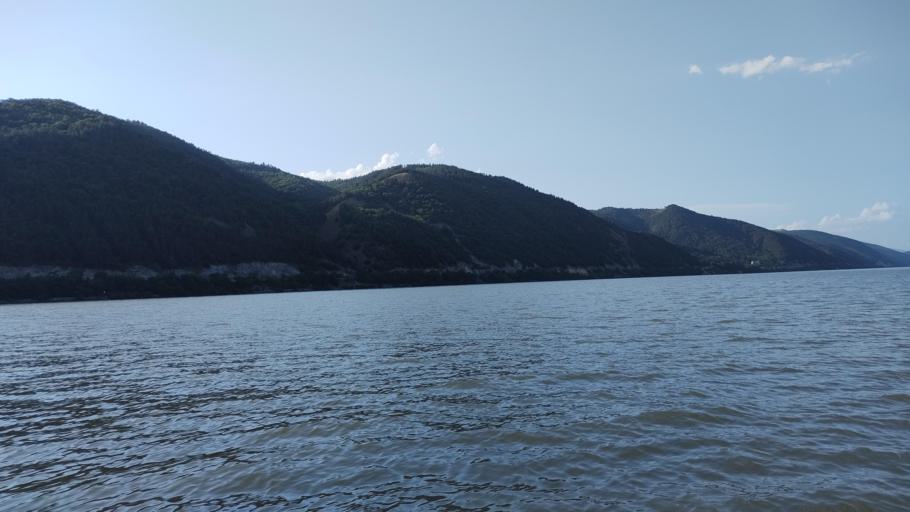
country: RO
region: Mehedinti
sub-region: Comuna Svinita
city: Svinita
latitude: 44.5005
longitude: 22.1919
